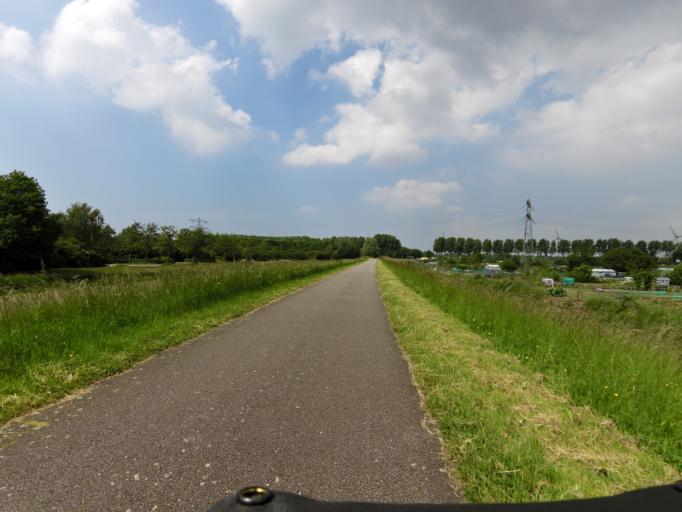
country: NL
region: South Holland
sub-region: Gemeente Maassluis
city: Maassluis
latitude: 51.8550
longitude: 4.2478
